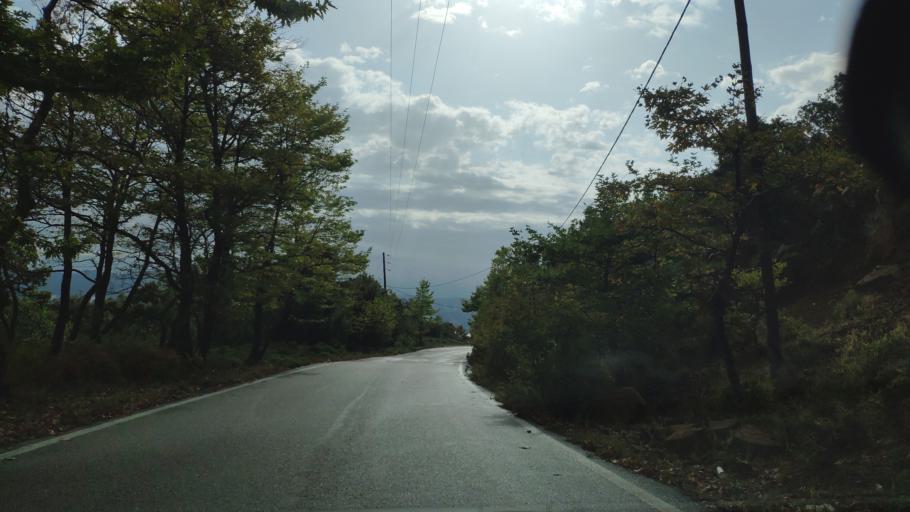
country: GR
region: West Greece
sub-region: Nomos Aitolias kai Akarnanias
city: Sardinia
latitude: 38.8644
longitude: 21.2999
